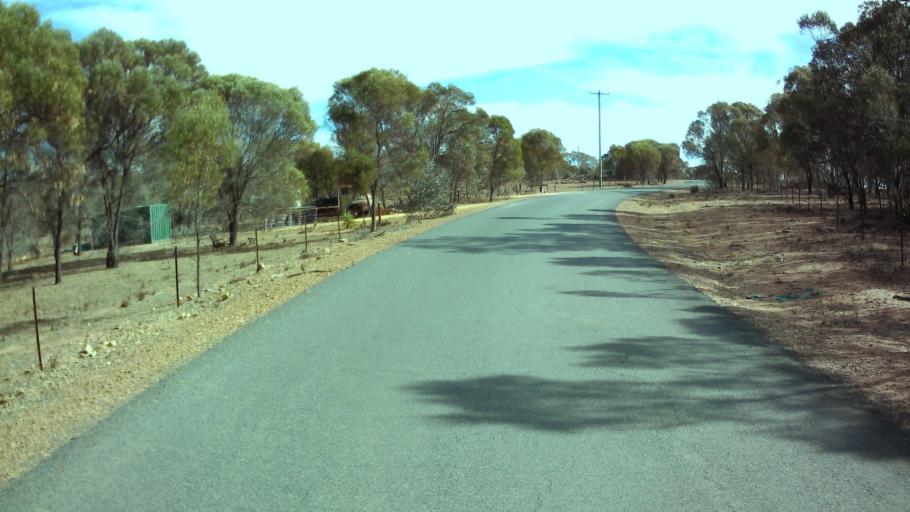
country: AU
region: New South Wales
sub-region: Weddin
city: Grenfell
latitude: -33.8775
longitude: 148.1924
